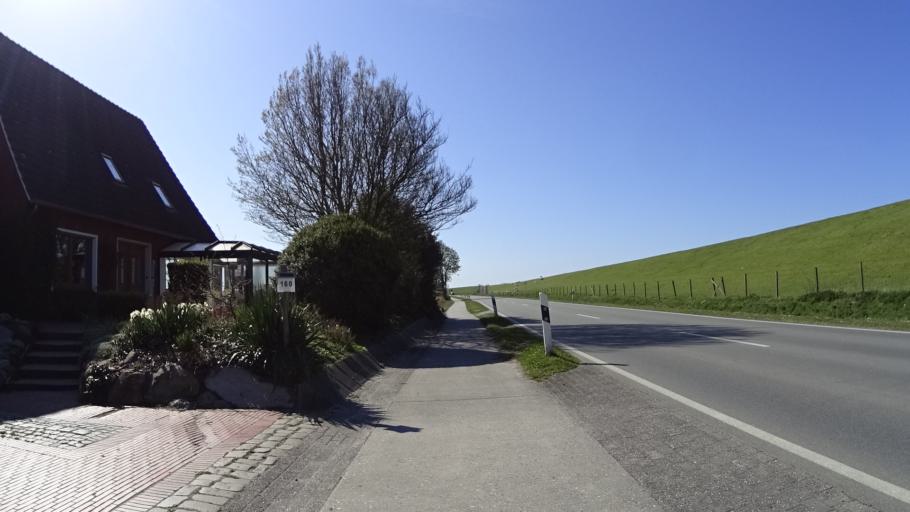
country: DE
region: Lower Saxony
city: Jemgum
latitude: 53.2439
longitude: 7.4076
